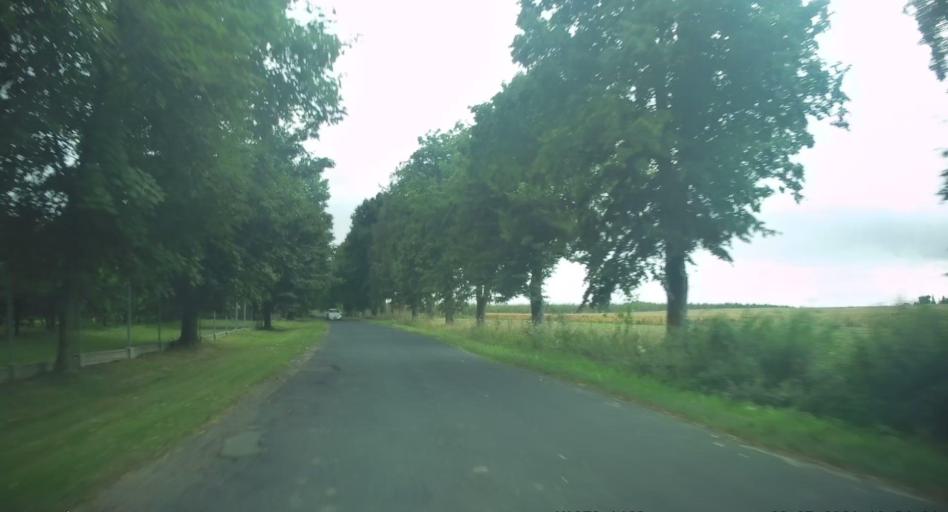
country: PL
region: Lodz Voivodeship
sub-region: Powiat rawski
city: Rawa Mazowiecka
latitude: 51.7669
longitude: 20.1835
